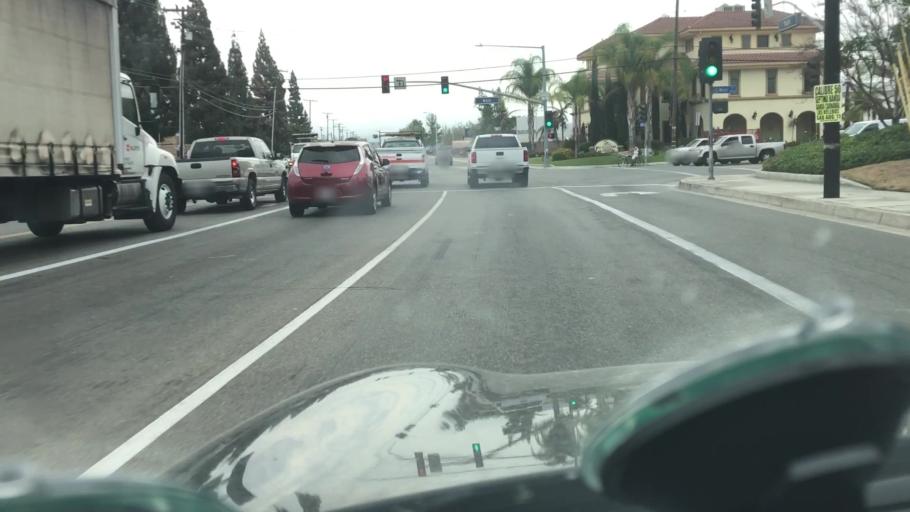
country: US
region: California
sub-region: Orange County
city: Orange
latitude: 33.8156
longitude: -117.8678
